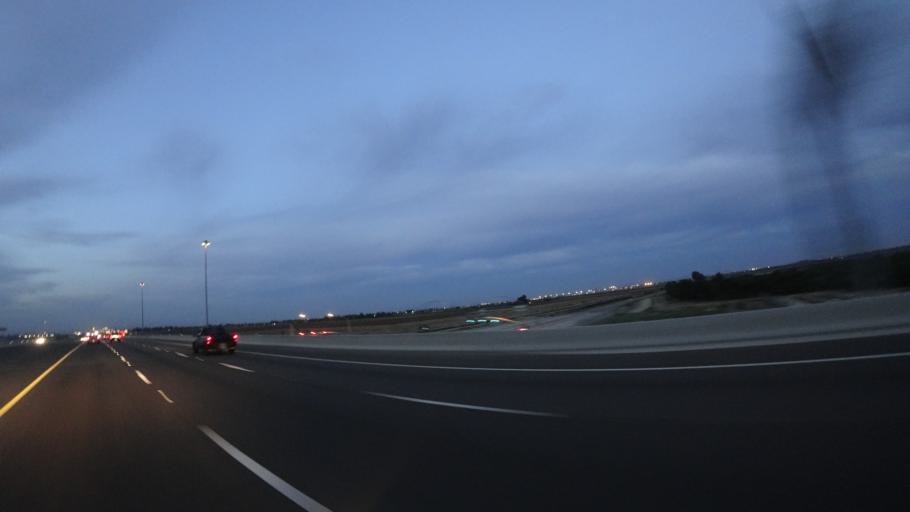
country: US
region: Arizona
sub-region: Maricopa County
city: Citrus Park
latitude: 33.5219
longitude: -112.4185
